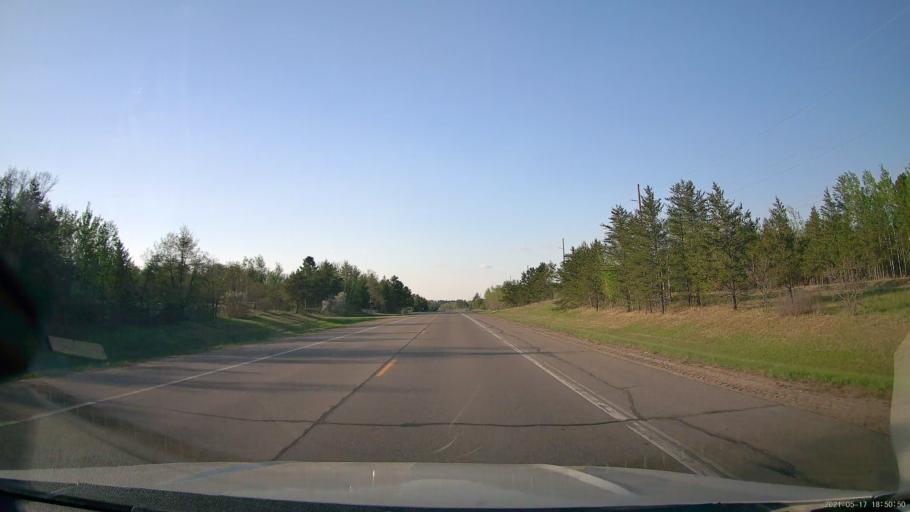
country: US
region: Minnesota
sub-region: Hubbard County
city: Park Rapids
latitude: 46.9408
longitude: -95.0166
